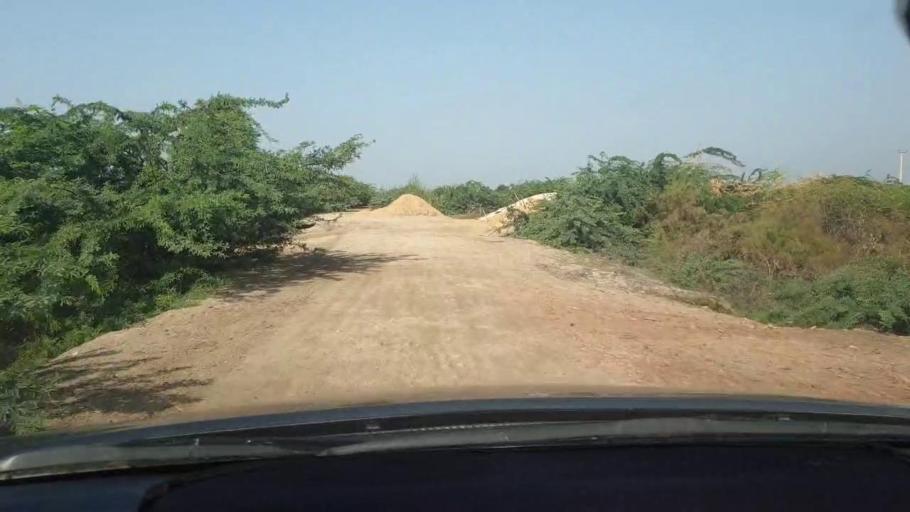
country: PK
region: Sindh
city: Tando Bago
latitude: 24.6801
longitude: 69.1353
